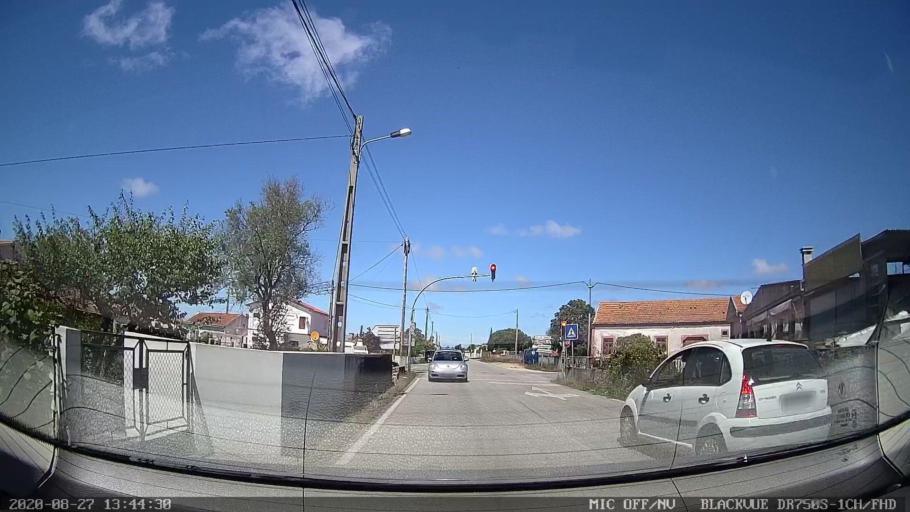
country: PT
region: Coimbra
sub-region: Mira
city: Mira
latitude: 40.4135
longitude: -8.7354
